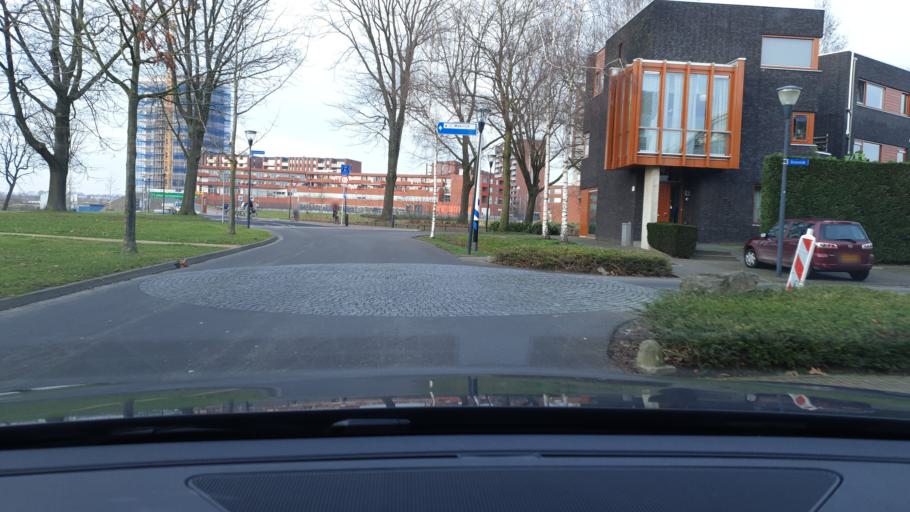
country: NL
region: North Brabant
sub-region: Gemeente Eindhoven
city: Meerhoven
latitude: 51.4396
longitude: 5.4096
